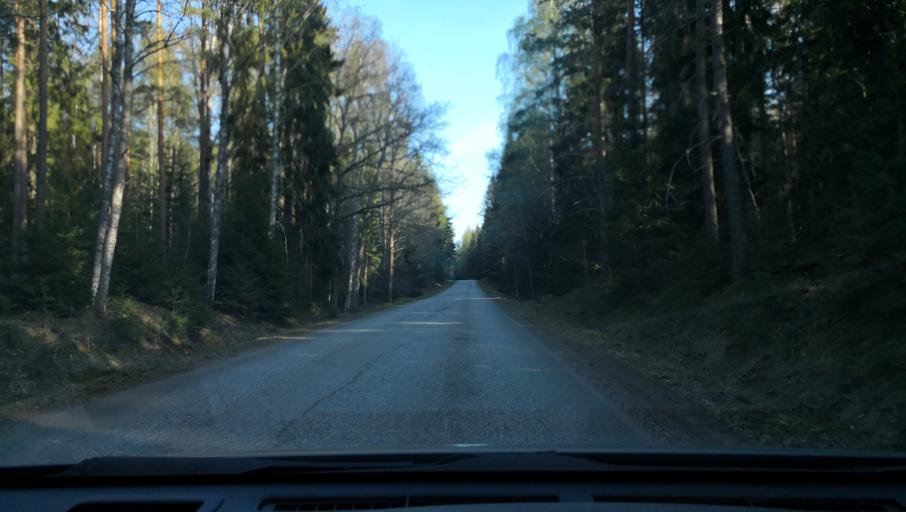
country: SE
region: Uppsala
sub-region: Heby Kommun
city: Tarnsjo
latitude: 60.2798
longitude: 16.8894
